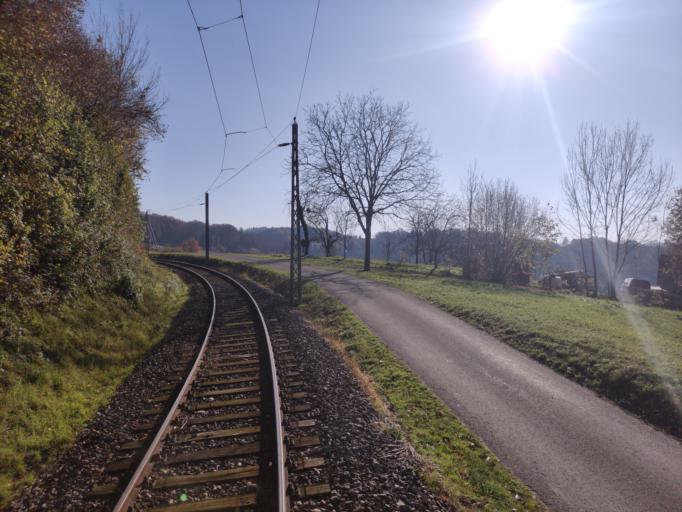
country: AT
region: Styria
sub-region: Politischer Bezirk Suedoststeiermark
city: Maierdorf
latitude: 46.8980
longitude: 15.8328
